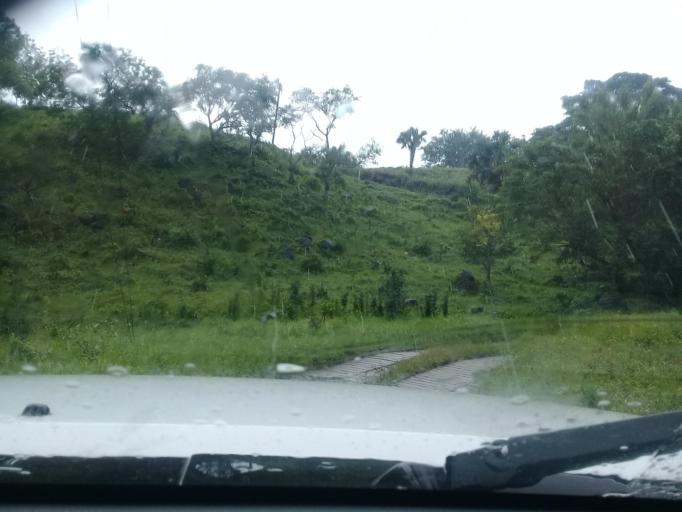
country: MX
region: Veracruz
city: Santiago Tuxtla
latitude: 18.4605
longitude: -95.3248
